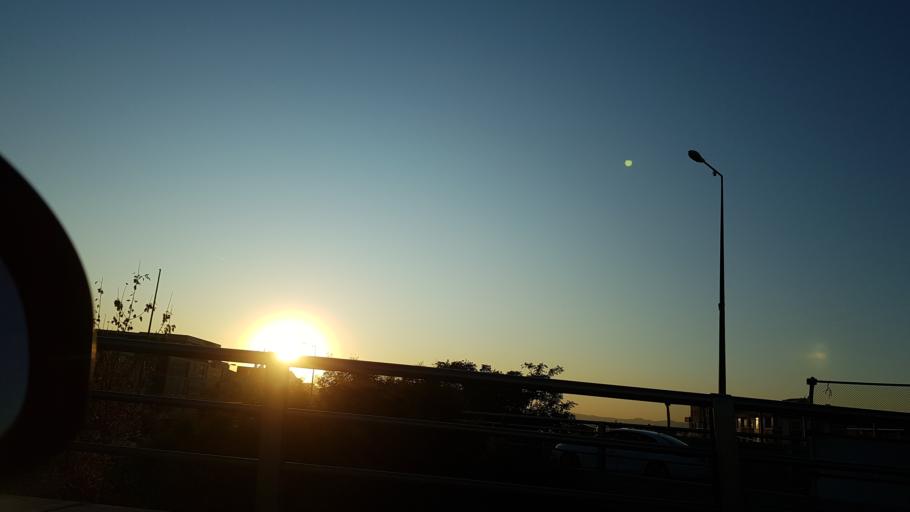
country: TR
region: Ankara
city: Etimesgut
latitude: 39.9482
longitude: 32.6686
